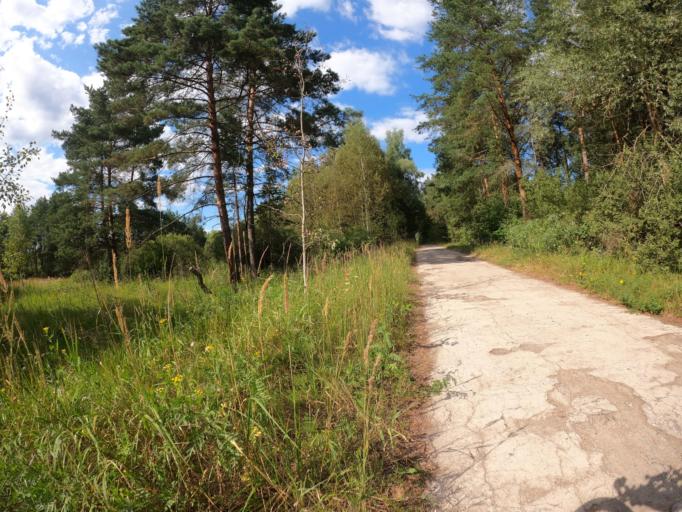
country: RU
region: Moskovskaya
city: Lopatinskiy
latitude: 55.3833
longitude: 38.7073
